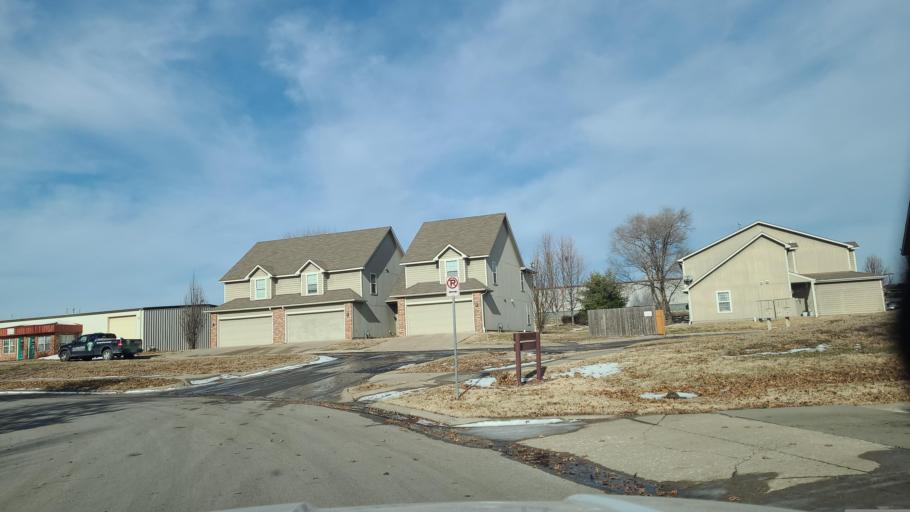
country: US
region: Kansas
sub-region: Douglas County
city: Lawrence
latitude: 38.9407
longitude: -95.2167
